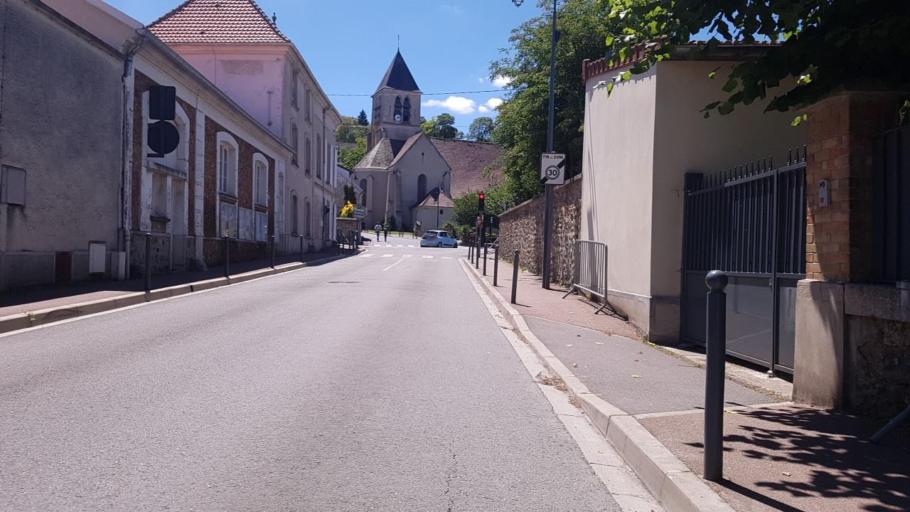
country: FR
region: Ile-de-France
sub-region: Departement de Seine-et-Marne
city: Saint-Jean-les-Deux-Jumeaux
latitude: 48.9518
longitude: 3.0191
